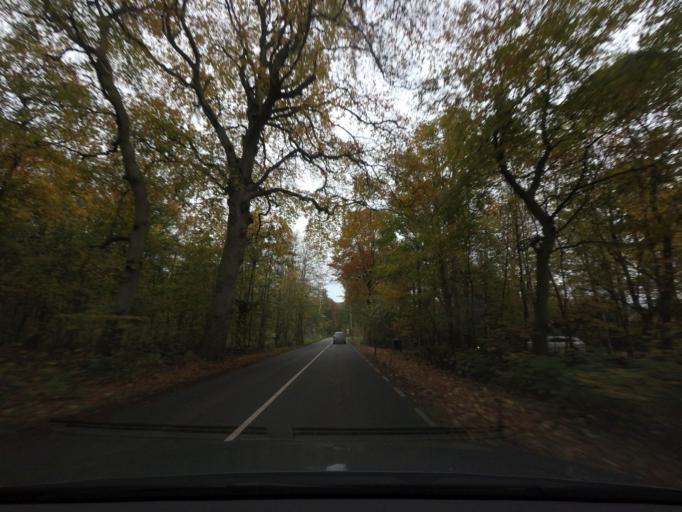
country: NL
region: North Holland
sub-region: Gemeente Bergen
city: Egmond aan Zee
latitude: 52.6545
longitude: 4.6614
